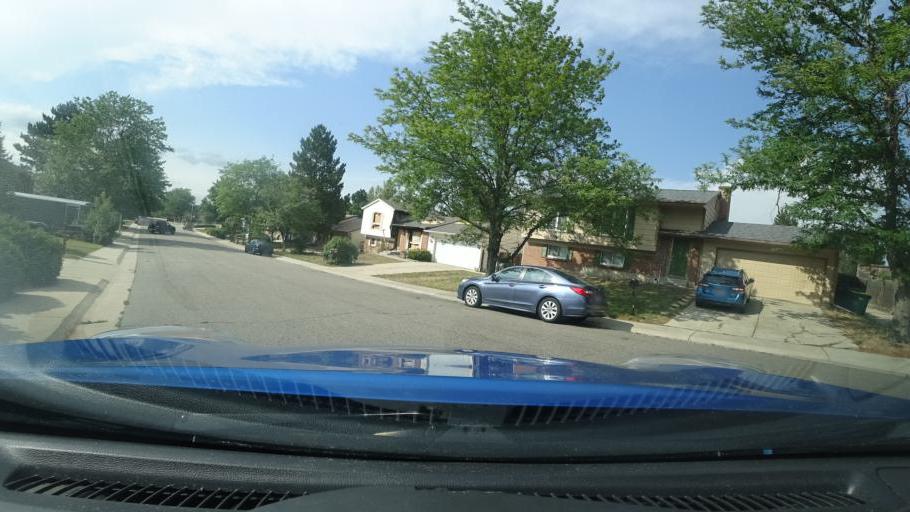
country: US
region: Colorado
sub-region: Adams County
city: Aurora
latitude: 39.6906
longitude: -104.7927
